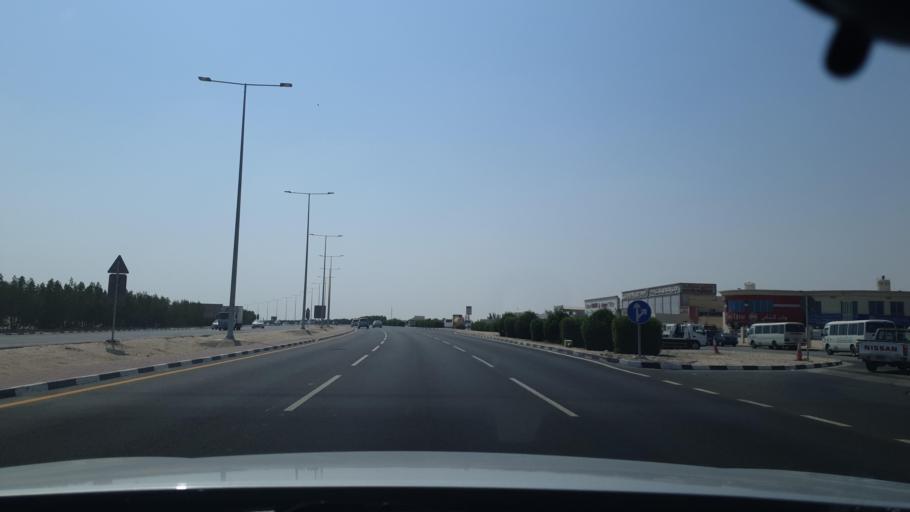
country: QA
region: Al Khawr
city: Al Khawr
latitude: 25.7127
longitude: 51.5078
